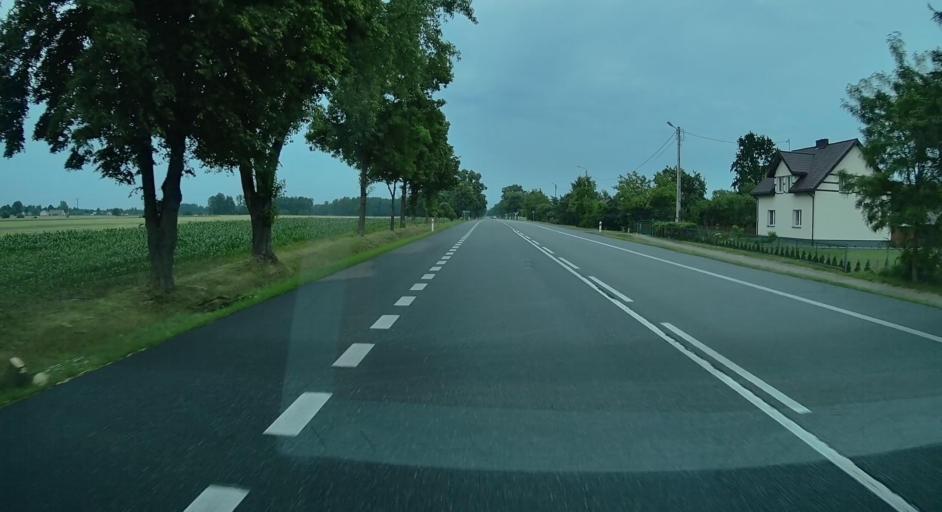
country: PL
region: Lublin Voivodeship
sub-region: Powiat lukowski
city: Trzebieszow
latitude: 52.0675
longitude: 22.5327
